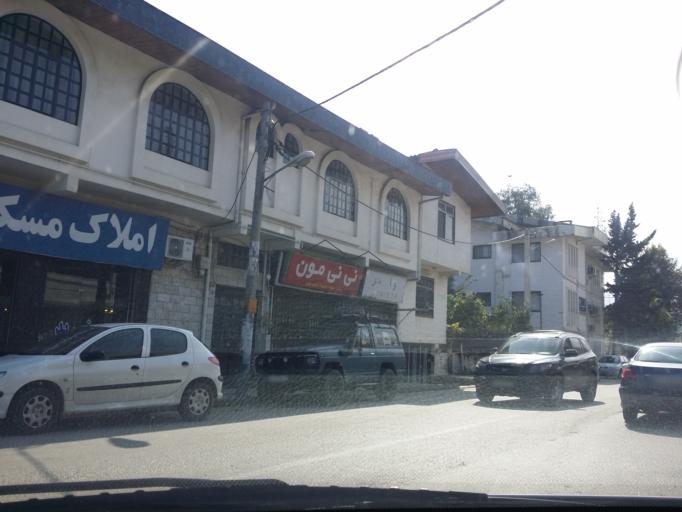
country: IR
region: Mazandaran
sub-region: Nowshahr
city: Nowshahr
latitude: 36.6556
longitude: 51.4886
